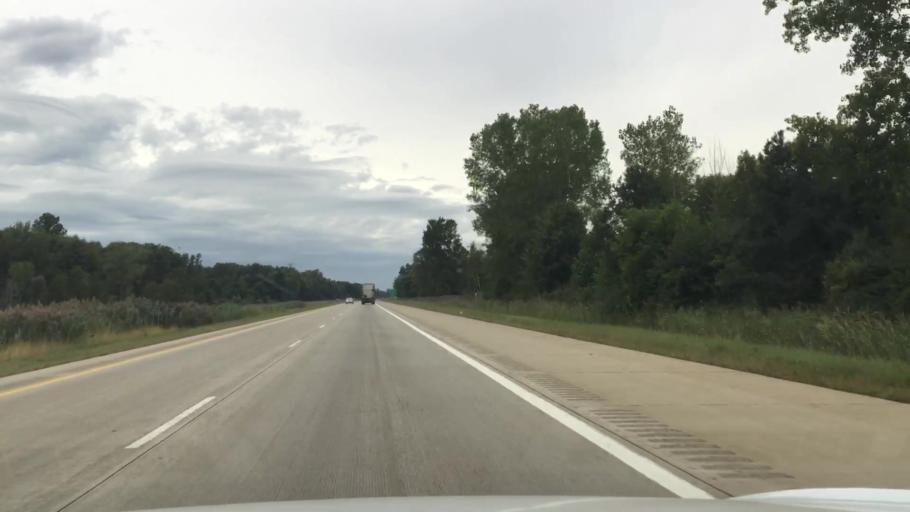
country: US
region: Michigan
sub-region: Saint Clair County
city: Saint Clair
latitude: 42.8284
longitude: -82.6054
